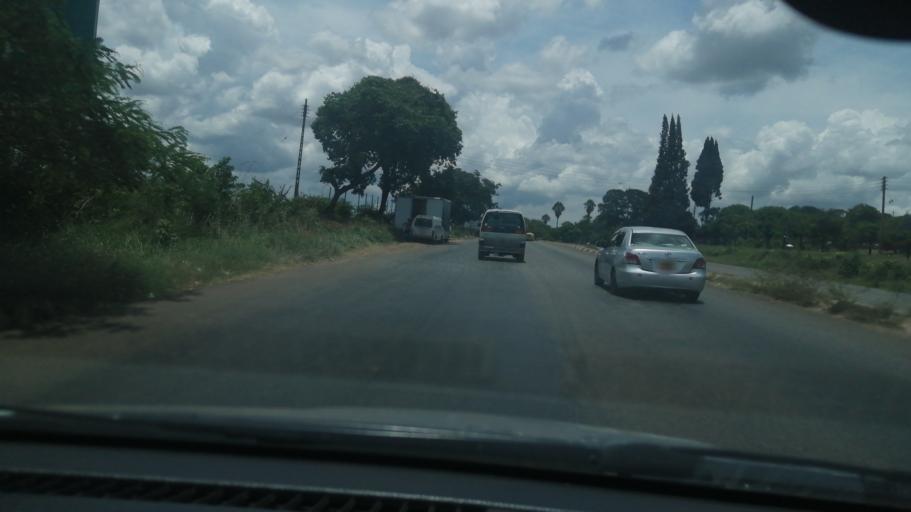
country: ZW
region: Harare
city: Harare
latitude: -17.8206
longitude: 30.9447
